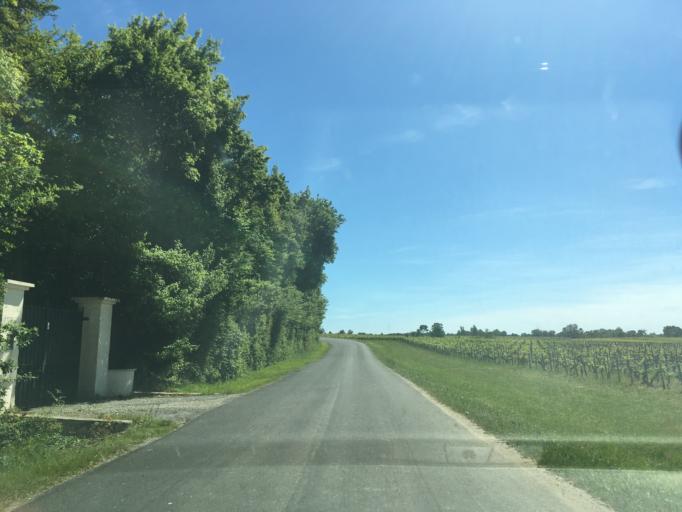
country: FR
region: Aquitaine
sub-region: Departement de la Gironde
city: Lesparre-Medoc
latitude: 45.3167
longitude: -0.8812
